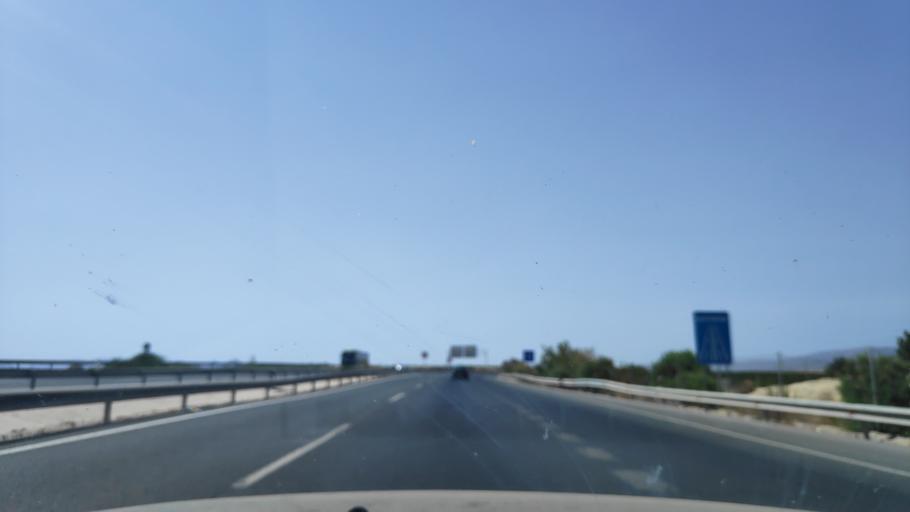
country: ES
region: Murcia
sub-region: Murcia
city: Lorqui
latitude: 38.1052
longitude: -1.2363
